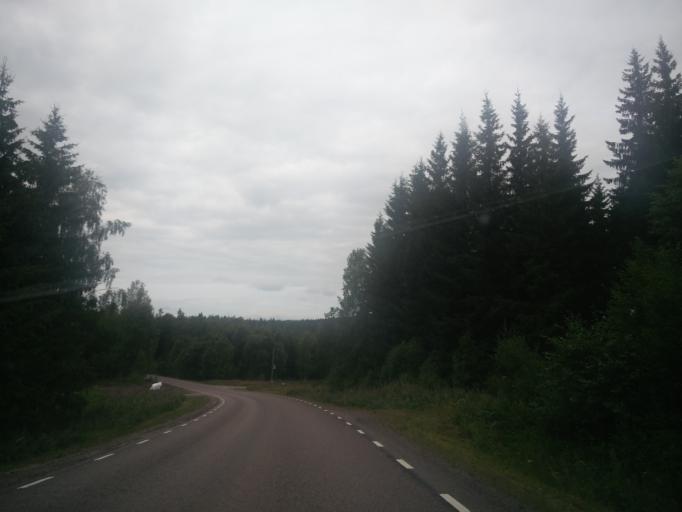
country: SE
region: Vaermland
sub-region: Torsby Kommun
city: Torsby
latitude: 59.9500
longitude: 12.7367
